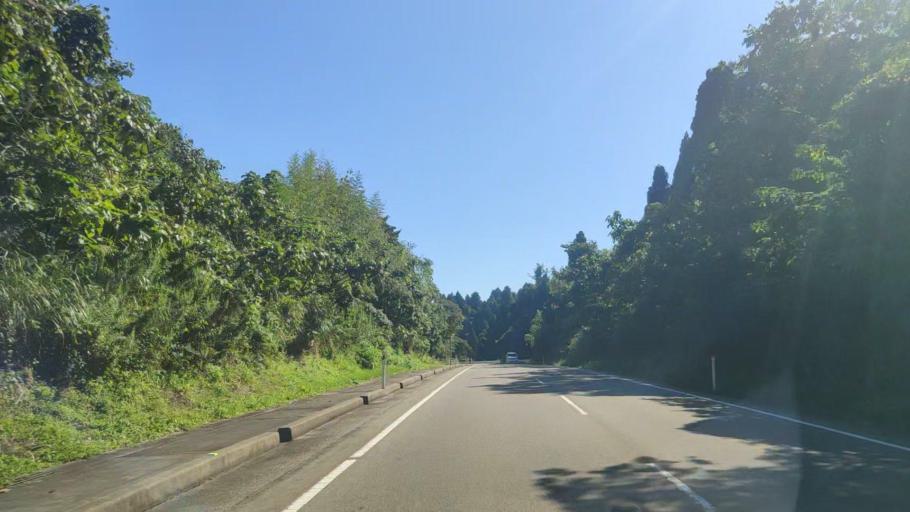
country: JP
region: Ishikawa
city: Nanao
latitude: 37.3795
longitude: 137.2337
